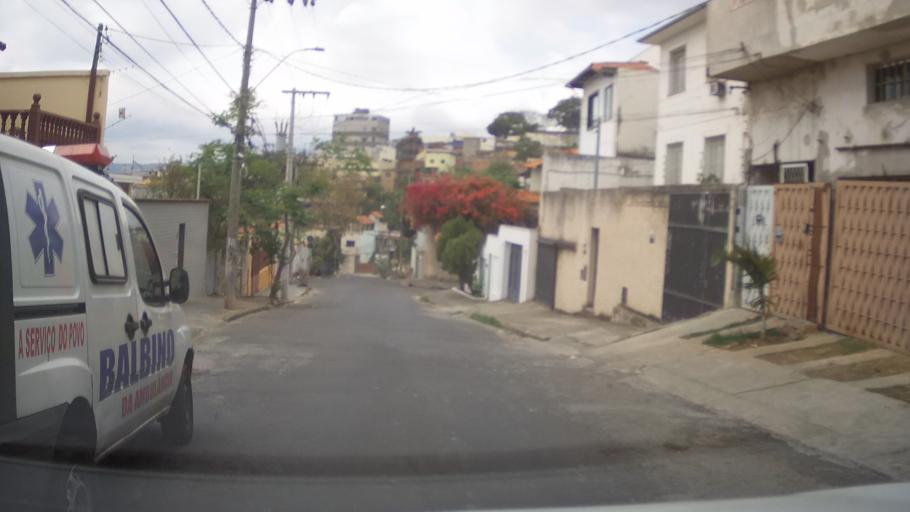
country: BR
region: Minas Gerais
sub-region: Belo Horizonte
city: Belo Horizonte
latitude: -19.9016
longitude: -43.9412
